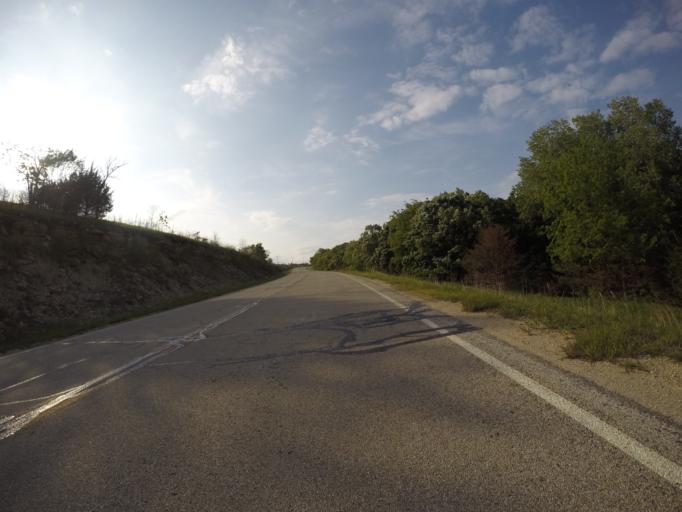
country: US
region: Kansas
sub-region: Pottawatomie County
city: Westmoreland
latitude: 39.4004
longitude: -96.6033
